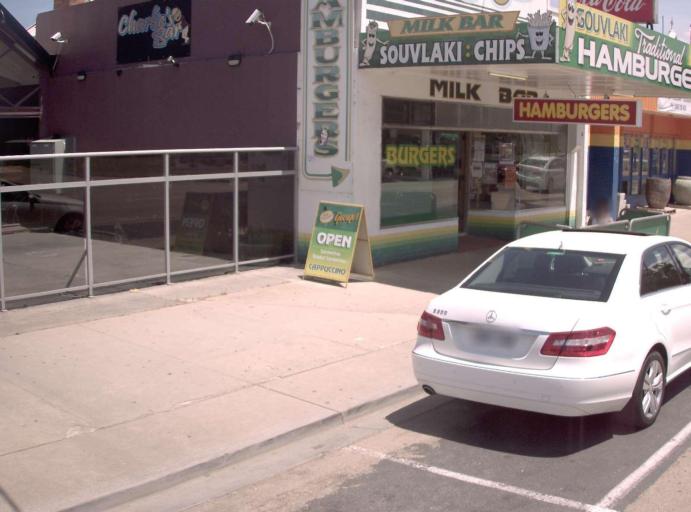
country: AU
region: Victoria
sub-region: East Gippsland
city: Bairnsdale
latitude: -37.8269
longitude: 147.6279
